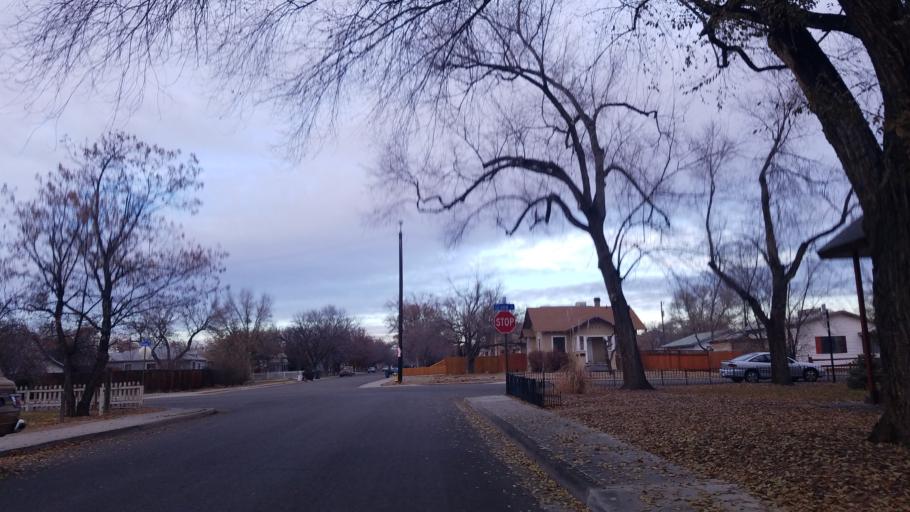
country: US
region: Colorado
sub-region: Mesa County
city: Grand Junction
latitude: 39.0699
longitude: -108.5453
